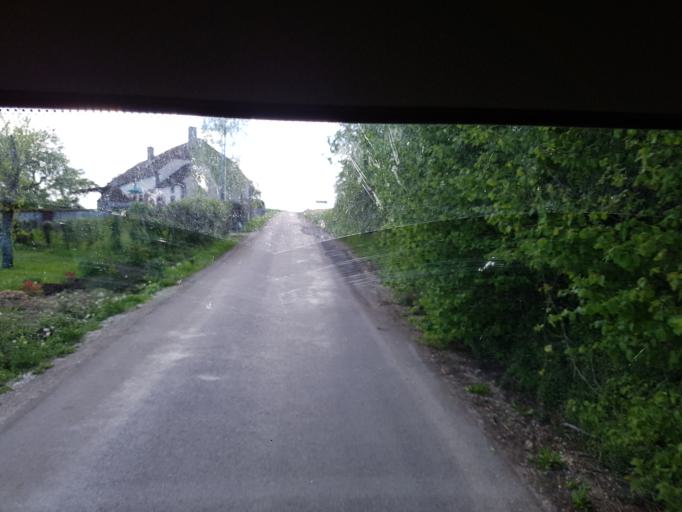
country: FR
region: Bourgogne
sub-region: Departement de l'Yonne
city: Neuvy-Sautour
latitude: 48.0548
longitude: 3.7685
